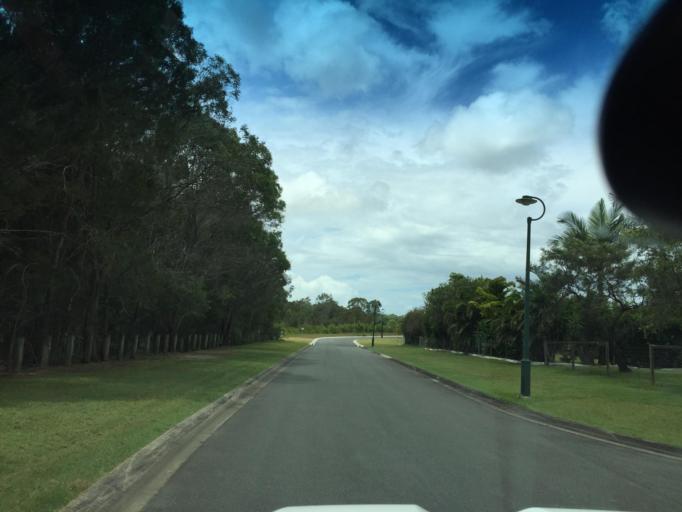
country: AU
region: Queensland
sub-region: Moreton Bay
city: Caboolture
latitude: -27.0395
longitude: 152.9249
